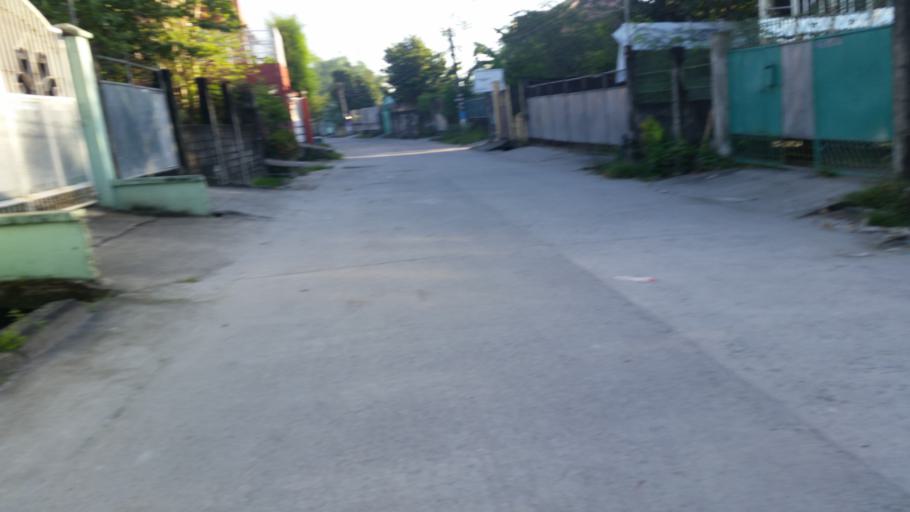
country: PH
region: Central Luzon
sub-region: Province of Pampanga
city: Mabalacat City
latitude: 15.2754
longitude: 120.5695
